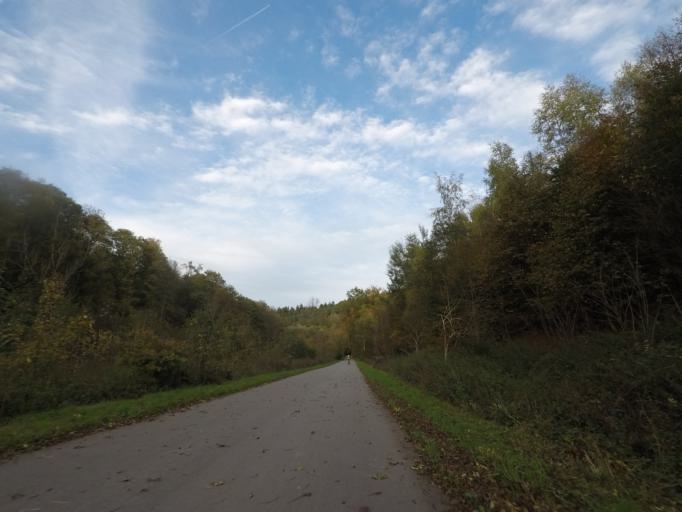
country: LU
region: Luxembourg
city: Itzig
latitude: 49.5927
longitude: 6.1583
